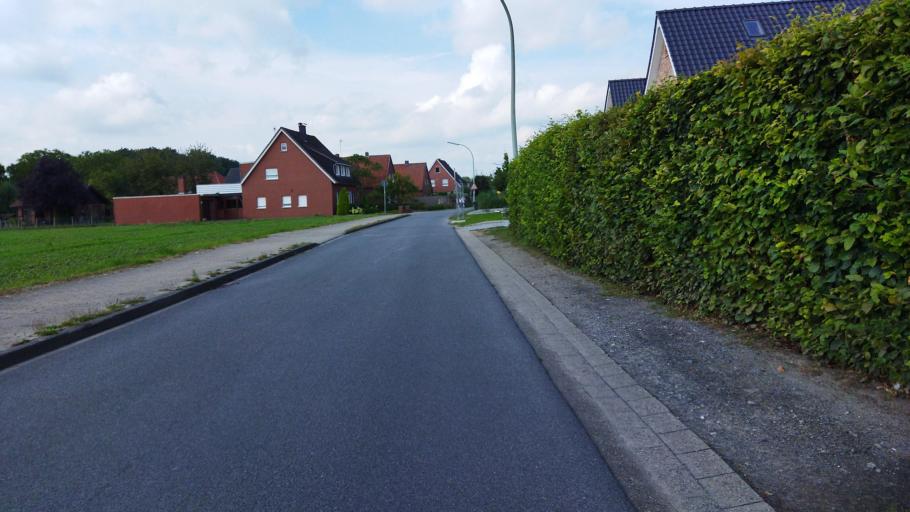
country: DE
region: North Rhine-Westphalia
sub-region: Regierungsbezirk Munster
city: Warendorf
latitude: 51.9571
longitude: 7.9654
